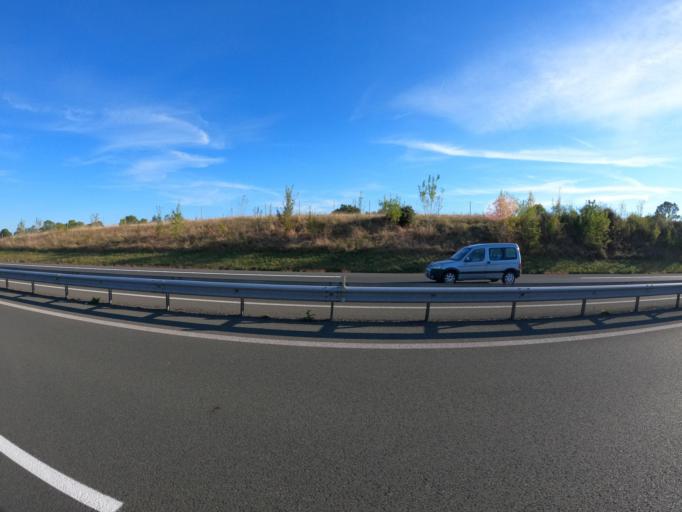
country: FR
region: Pays de la Loire
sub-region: Departement de Maine-et-Loire
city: Saint-Lambert-du-Lattay
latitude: 47.2416
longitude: -0.6422
